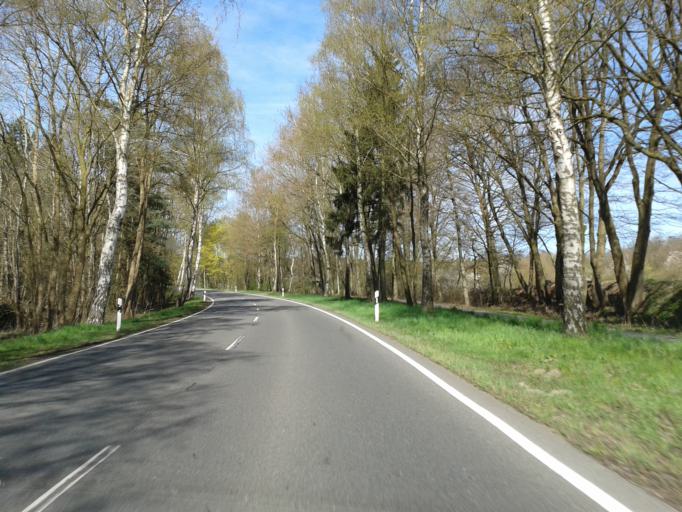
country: DE
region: Lower Saxony
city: Suderburg
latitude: 52.9562
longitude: 10.4775
